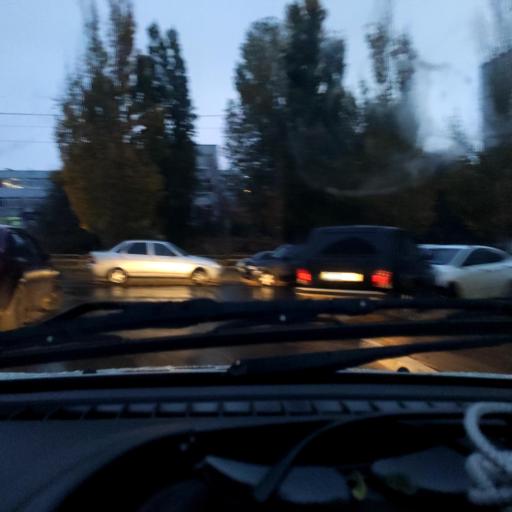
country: RU
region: Samara
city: Zhigulevsk
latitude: 53.4777
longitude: 49.4613
